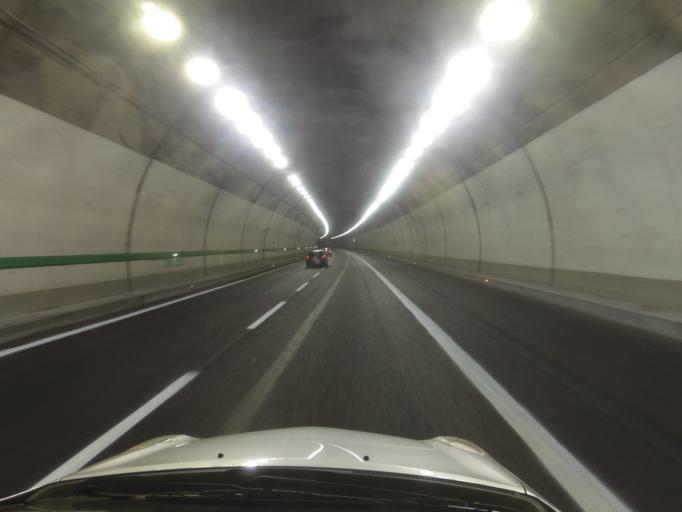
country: IT
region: Emilia-Romagna
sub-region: Provincia di Bologna
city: Grizzana
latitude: 44.2265
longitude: 11.1846
